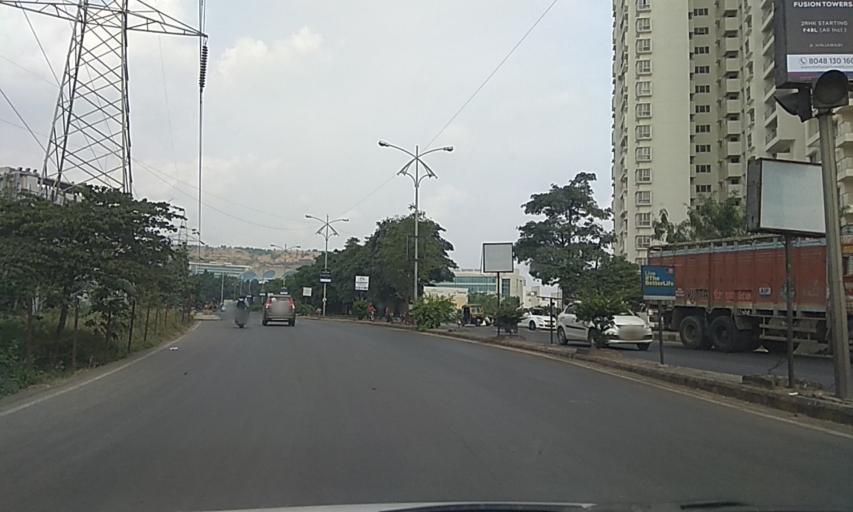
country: IN
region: Maharashtra
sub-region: Pune Division
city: Pimpri
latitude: 18.5912
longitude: 73.7069
